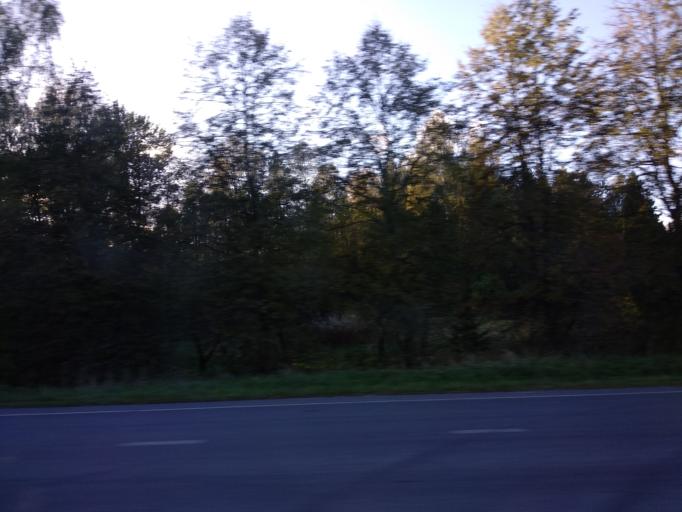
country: EE
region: Polvamaa
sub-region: Polva linn
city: Polva
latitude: 58.0420
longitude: 27.0658
